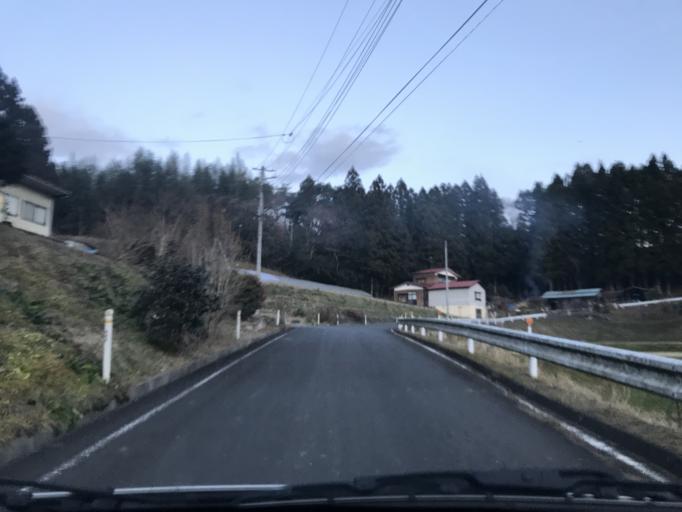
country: JP
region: Iwate
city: Ichinoseki
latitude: 38.8297
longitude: 141.0872
